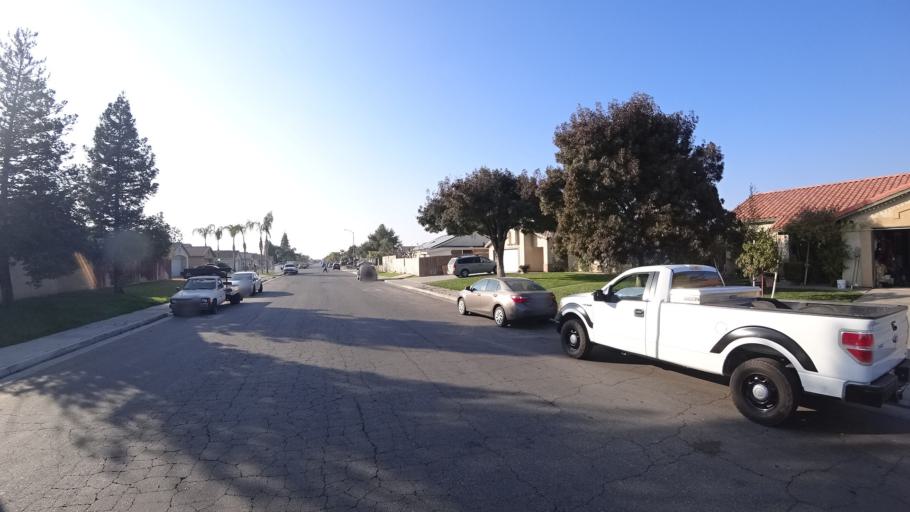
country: US
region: California
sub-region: Kern County
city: Greenfield
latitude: 35.2870
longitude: -119.0138
